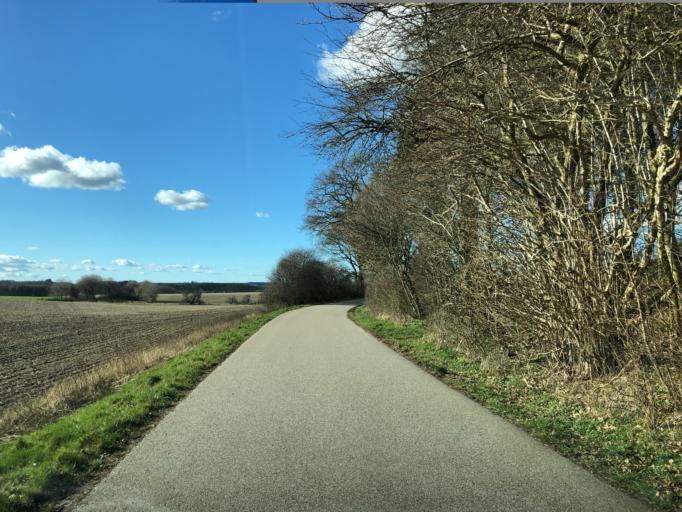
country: DK
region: Central Jutland
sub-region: Favrskov Kommune
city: Hammel
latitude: 56.3012
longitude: 9.9207
